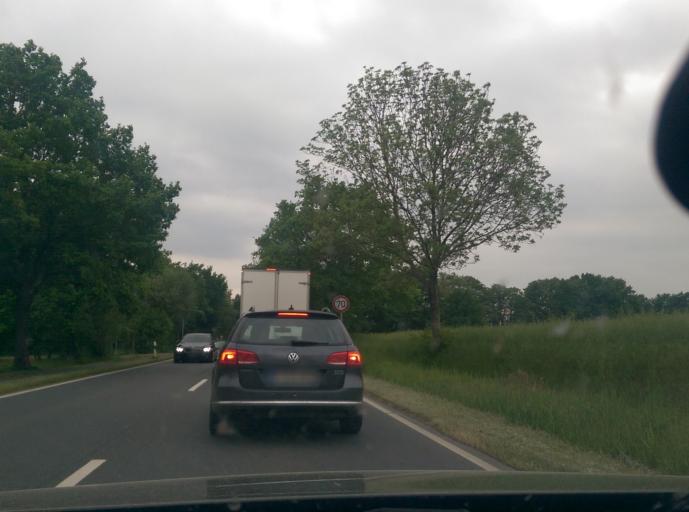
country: DE
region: Lower Saxony
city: Garbsen-Mitte
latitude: 52.4434
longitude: 9.5916
